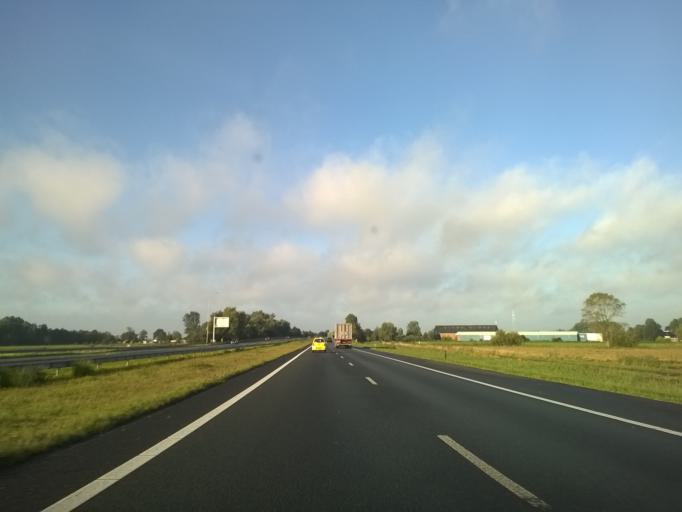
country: NL
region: Groningen
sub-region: Gemeente Zuidhorn
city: Aduard
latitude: 53.1986
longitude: 6.4554
